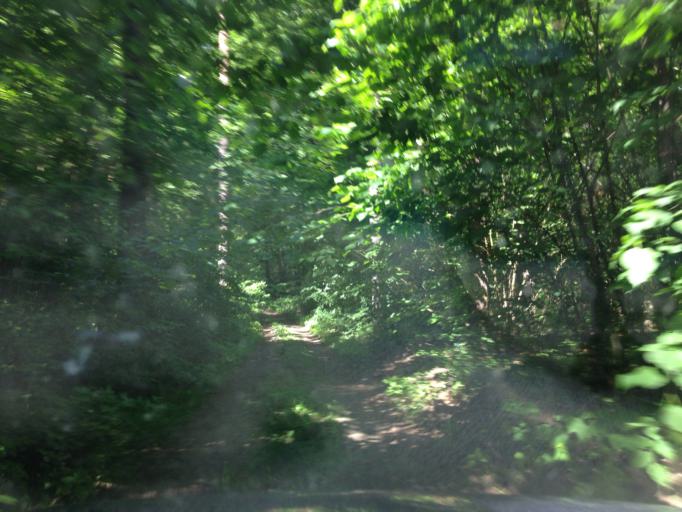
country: PL
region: Kujawsko-Pomorskie
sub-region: Powiat brodnicki
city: Bartniczka
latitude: 53.2672
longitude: 19.5761
